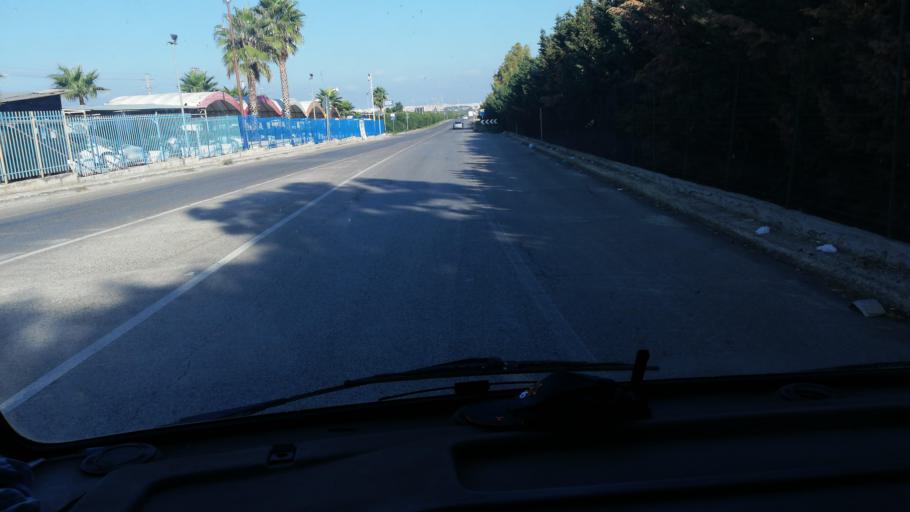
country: IT
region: Apulia
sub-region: Provincia di Bari
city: Palo del Colle
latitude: 41.0690
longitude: 16.7033
